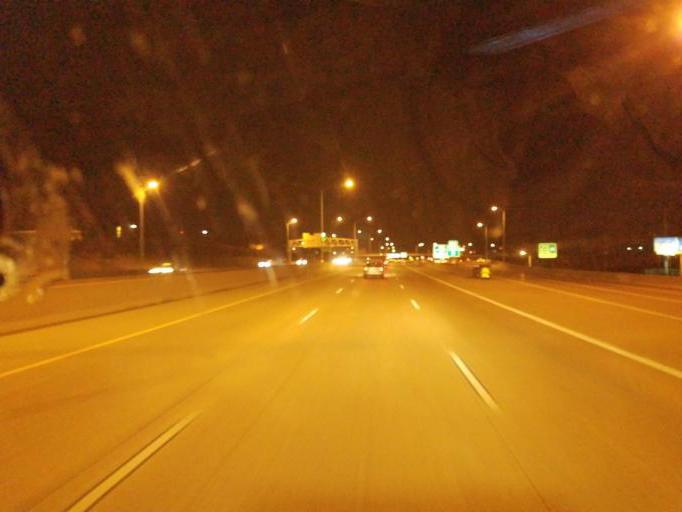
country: US
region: Iowa
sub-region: Polk County
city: Des Moines
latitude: 41.5959
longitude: -93.6348
